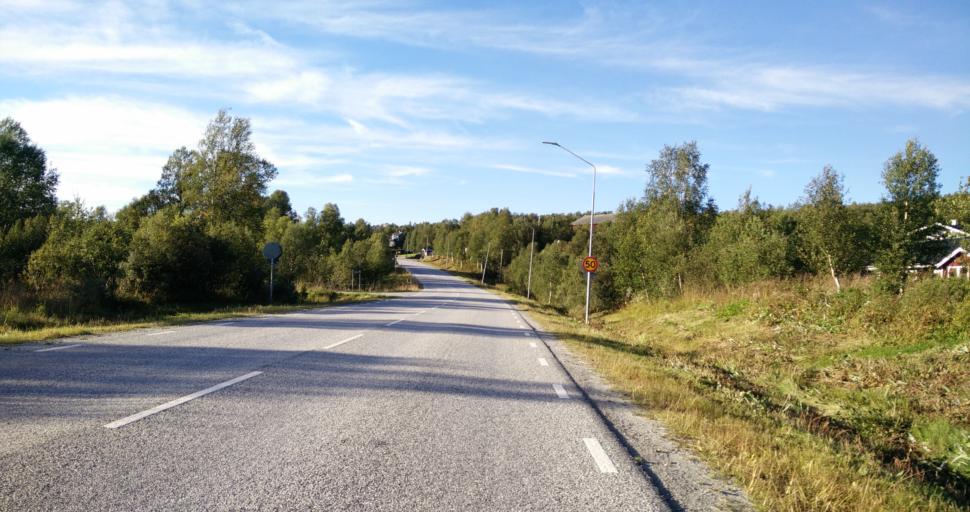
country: NO
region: Sor-Trondelag
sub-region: Tydal
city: Aas
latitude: 62.6347
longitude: 12.4450
